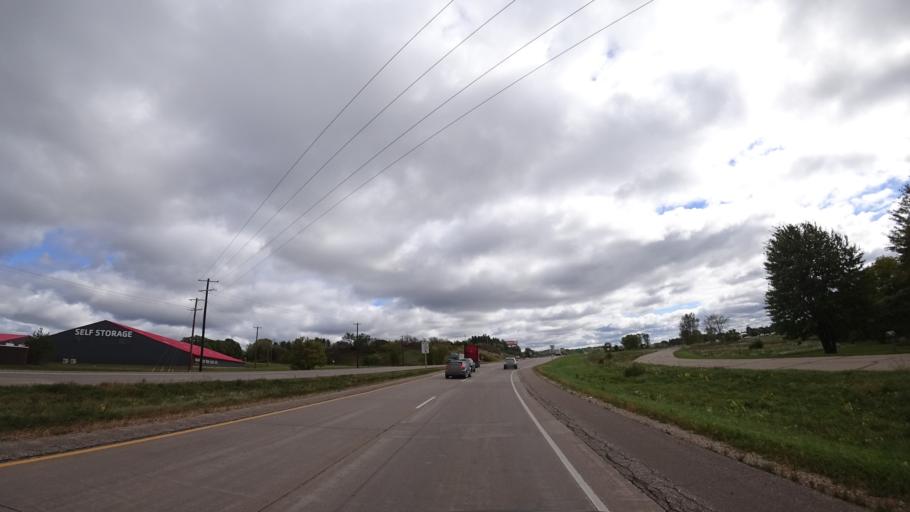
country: US
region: Wisconsin
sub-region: Eau Claire County
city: Eau Claire
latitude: 44.8431
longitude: -91.5578
